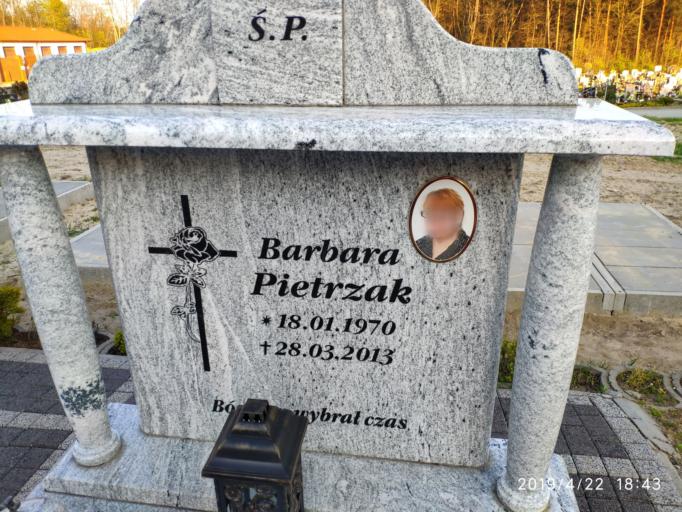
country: PL
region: Lubusz
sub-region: Zielona Gora
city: Zielona Gora
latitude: 51.9270
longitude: 15.5334
